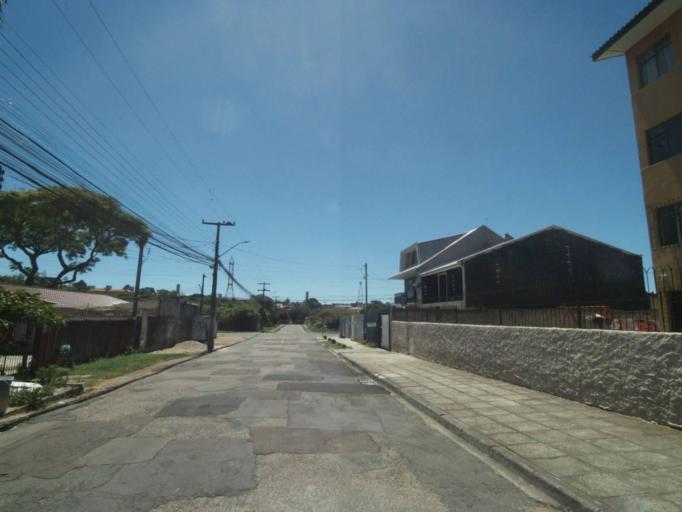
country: BR
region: Parana
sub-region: Curitiba
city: Curitiba
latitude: -25.4740
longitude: -49.3460
